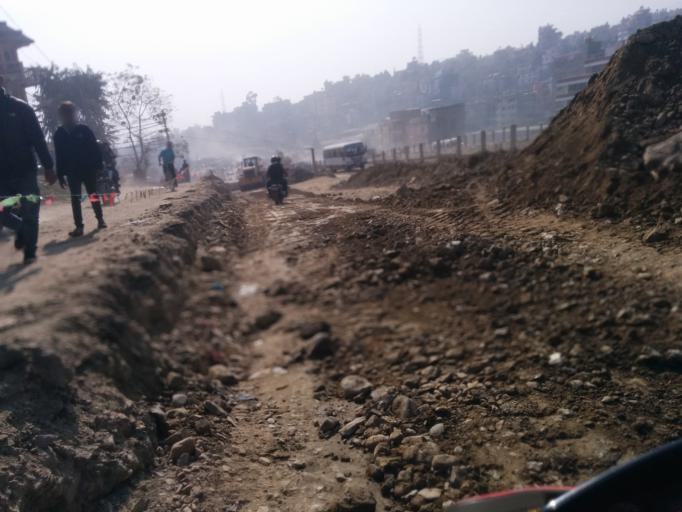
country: NP
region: Central Region
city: Kirtipur
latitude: 27.6921
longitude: 85.2824
